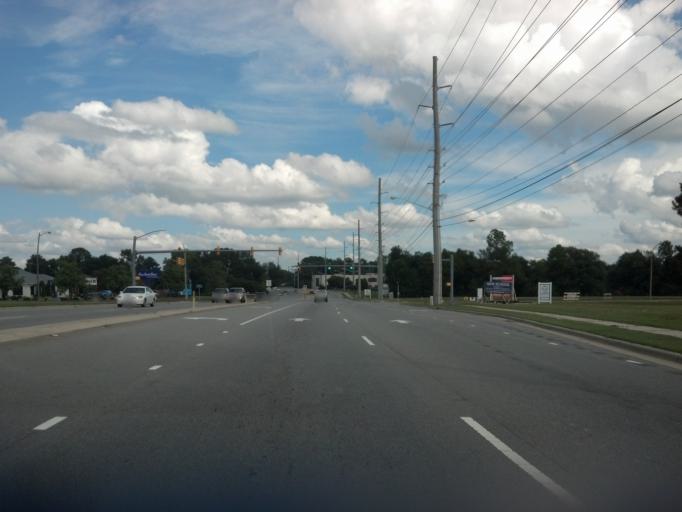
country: US
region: North Carolina
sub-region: Pitt County
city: Windsor
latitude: 35.5566
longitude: -77.3705
